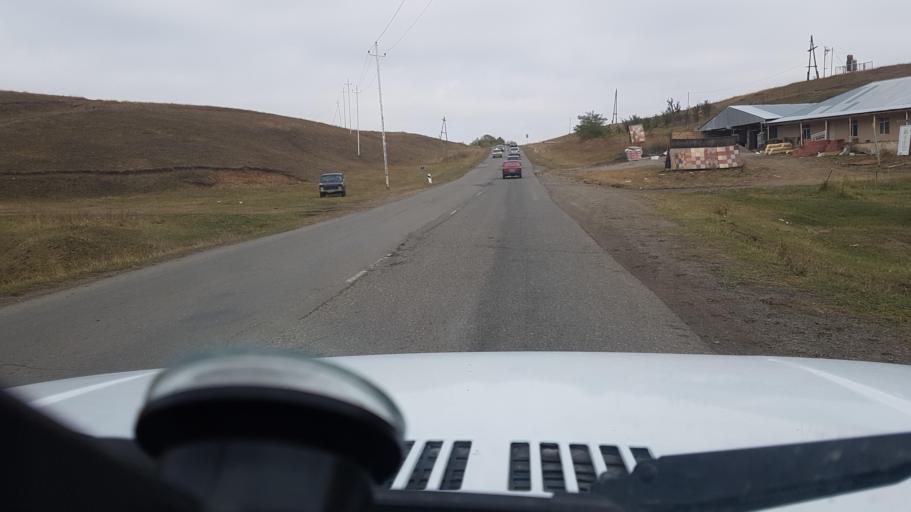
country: AZ
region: Gadabay Rayon
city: Ariqdam
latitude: 40.6178
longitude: 45.8110
